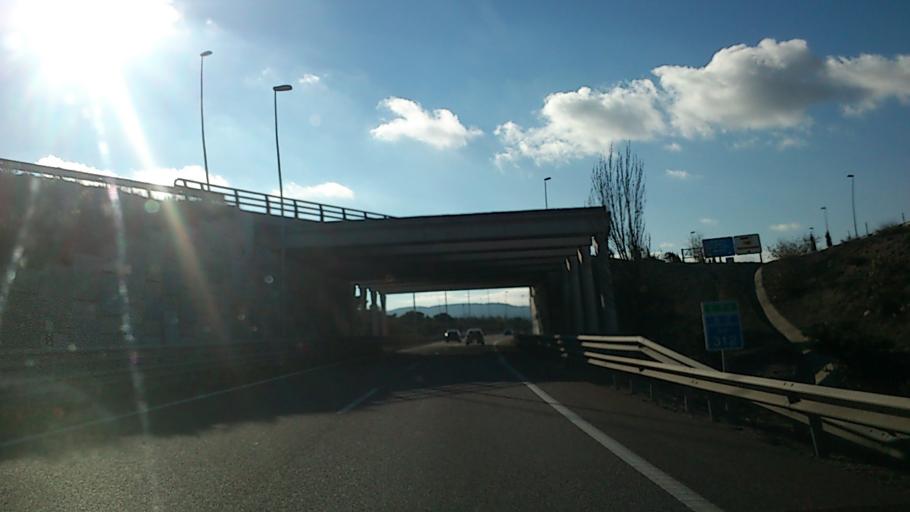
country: ES
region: Aragon
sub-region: Provincia de Zaragoza
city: Montecanal
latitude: 41.6353
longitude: -0.9765
